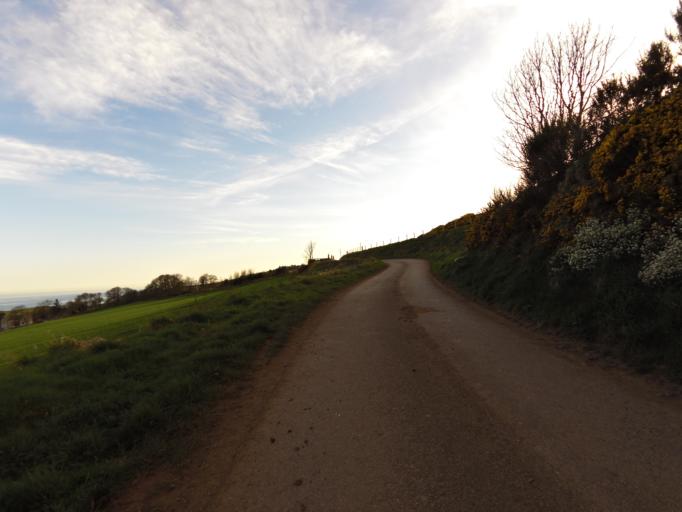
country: GB
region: Scotland
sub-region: Aberdeenshire
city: Inverbervie
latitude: 56.8685
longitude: -2.2388
